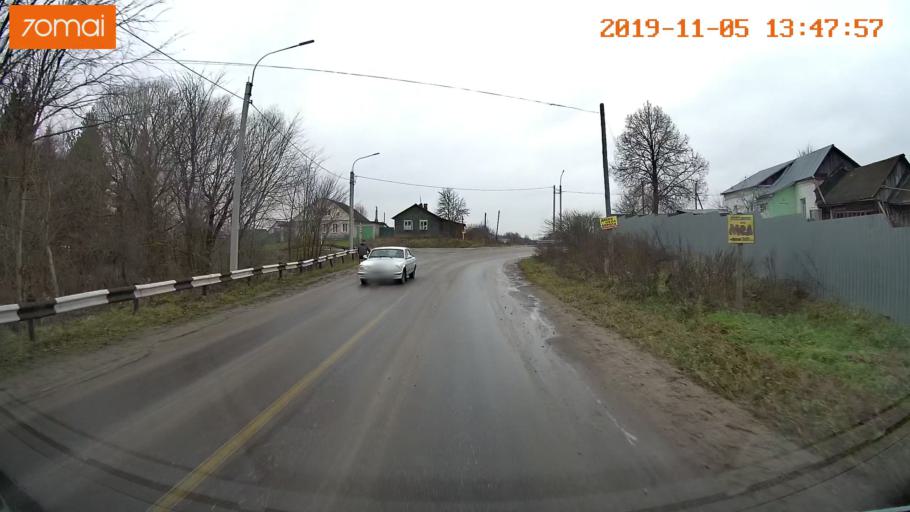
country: RU
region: Ivanovo
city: Shuya
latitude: 57.0013
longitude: 41.4060
